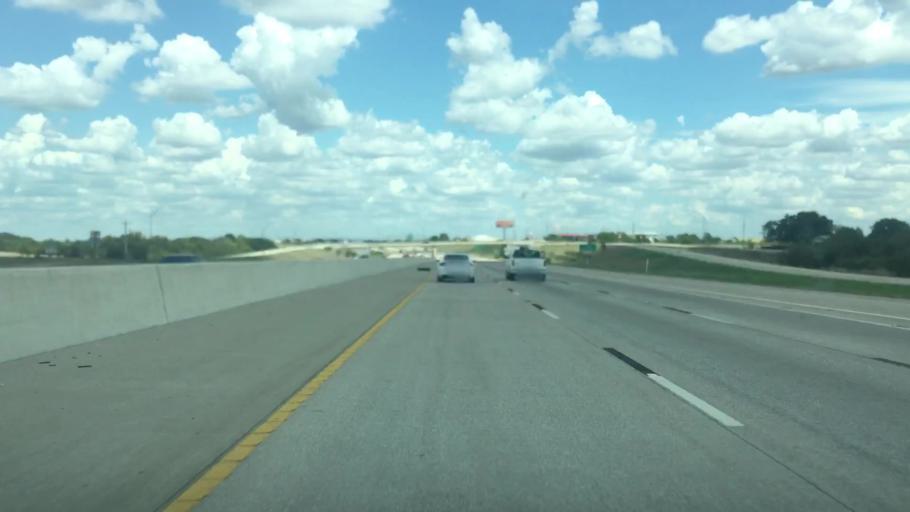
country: US
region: Texas
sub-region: Bell County
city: Salado
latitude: 30.9138
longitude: -97.5499
